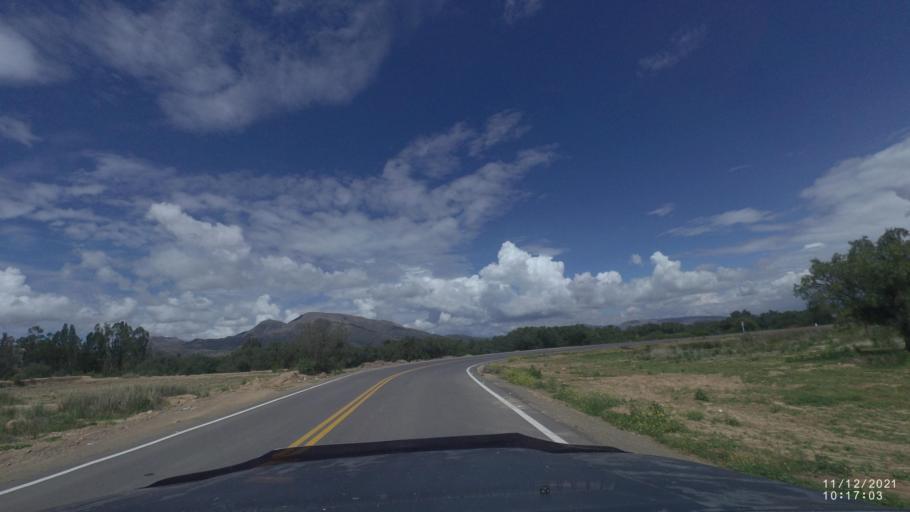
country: BO
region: Cochabamba
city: Tarata
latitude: -17.5898
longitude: -66.0196
